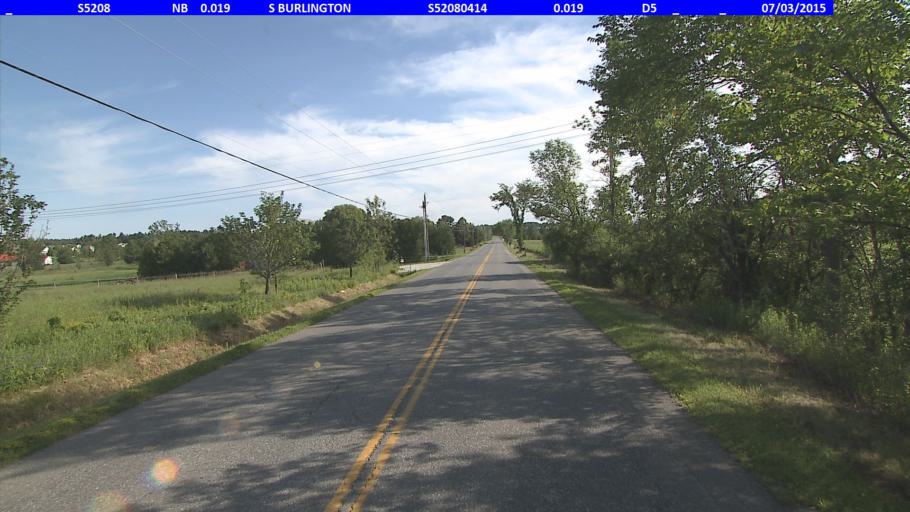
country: US
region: Vermont
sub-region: Chittenden County
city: South Burlington
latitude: 44.4116
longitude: -73.1766
